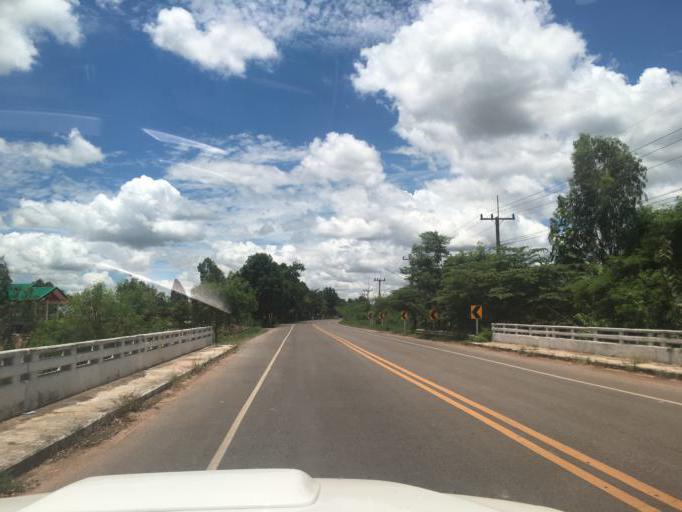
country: TH
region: Changwat Udon Thani
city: Nong Saeng
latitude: 17.1487
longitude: 102.7897
